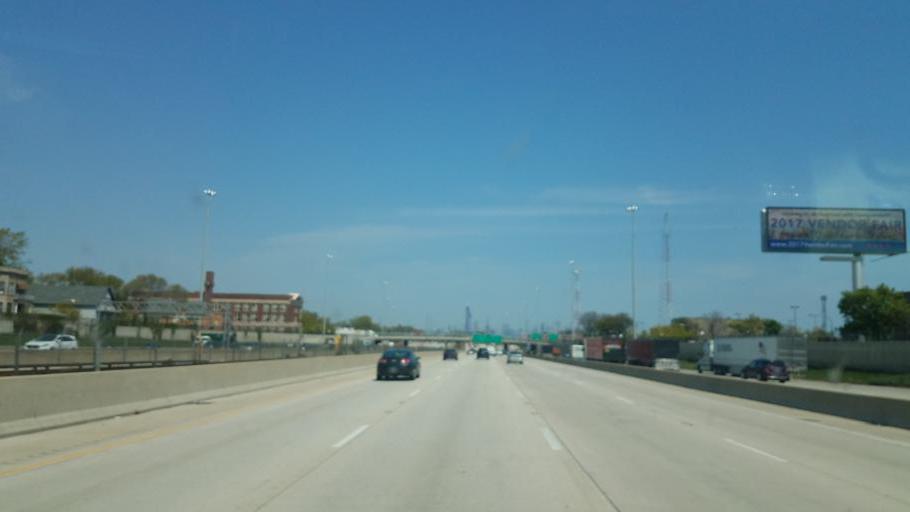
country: US
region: Illinois
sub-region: Cook County
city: Chicago
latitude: 41.7989
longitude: -87.6305
